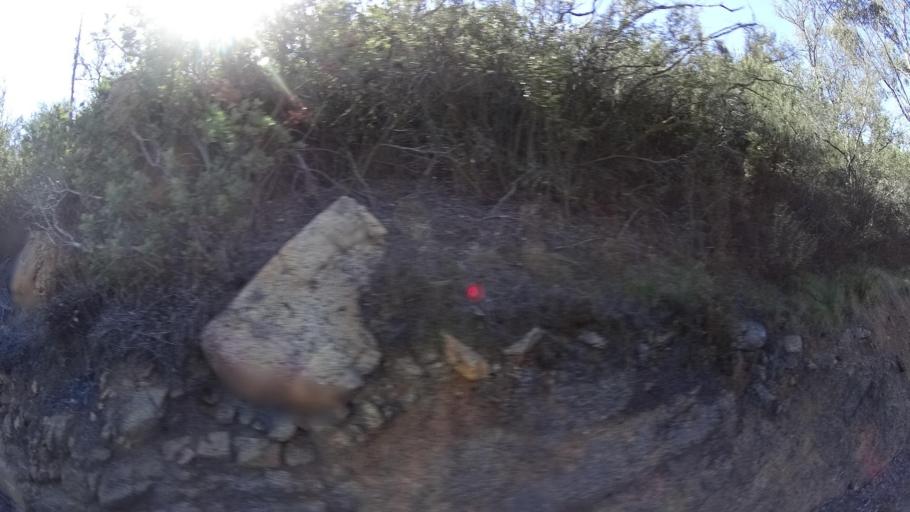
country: US
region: California
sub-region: San Diego County
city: Jamul
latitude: 32.7291
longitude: -116.8265
